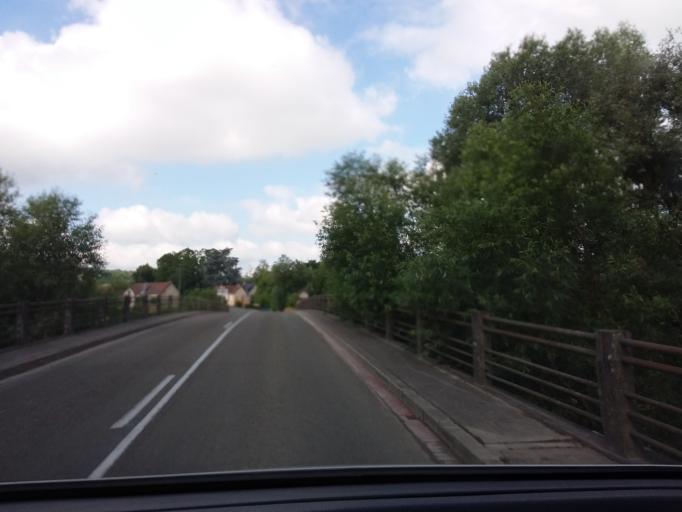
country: FR
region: Champagne-Ardenne
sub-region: Departement de la Marne
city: Fismes
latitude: 49.3818
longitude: 3.7324
